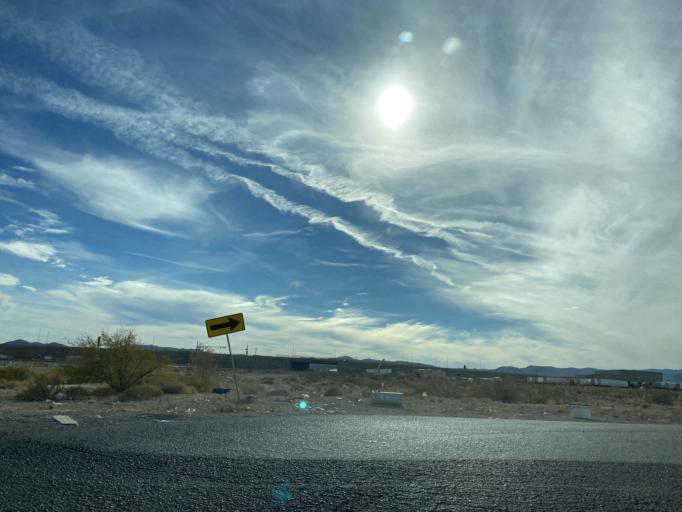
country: US
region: Nevada
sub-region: Clark County
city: Enterprise
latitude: 36.0297
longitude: -115.2258
